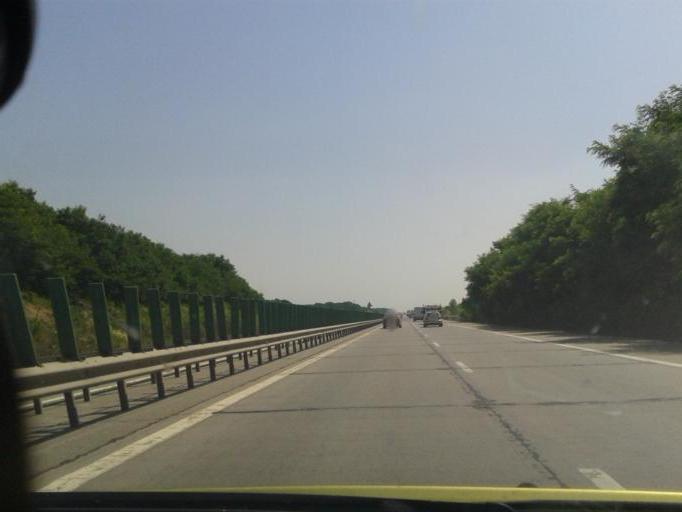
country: RO
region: Ilfov
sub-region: Comuna Cernica
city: Tanganu
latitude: 44.4163
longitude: 26.3085
